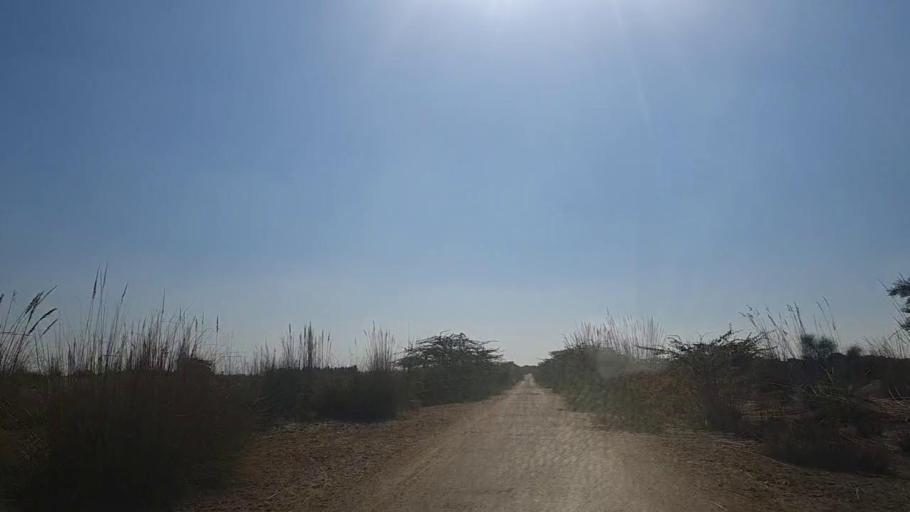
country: PK
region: Sindh
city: Khadro
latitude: 26.1612
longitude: 68.8380
